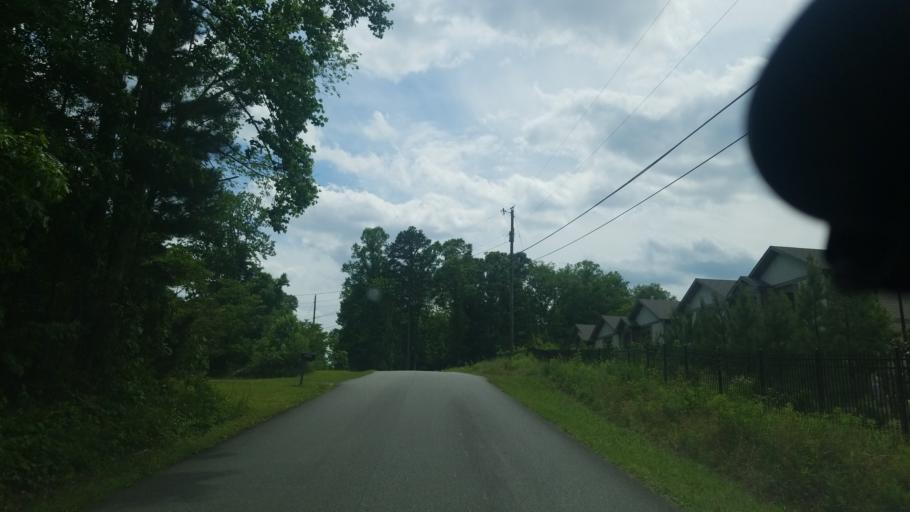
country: US
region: Georgia
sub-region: Forsyth County
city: Cumming
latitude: 34.1575
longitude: -84.1123
